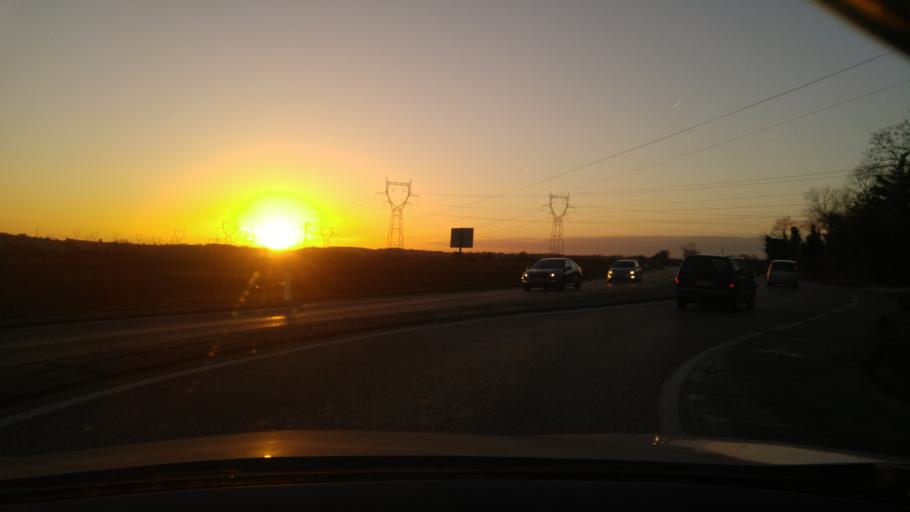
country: FR
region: Rhone-Alpes
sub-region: Departement de l'Isere
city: Tignieu-Jameyzieu
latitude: 45.7173
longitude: 5.1875
